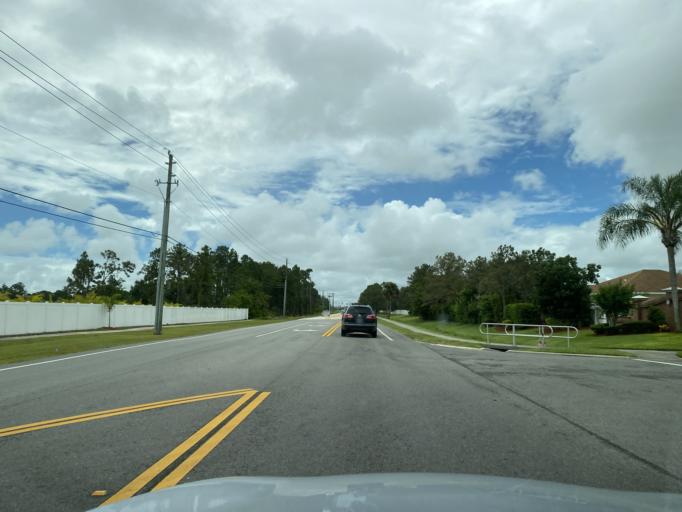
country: US
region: Florida
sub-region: Brevard County
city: West Melbourne
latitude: 28.0533
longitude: -80.6541
